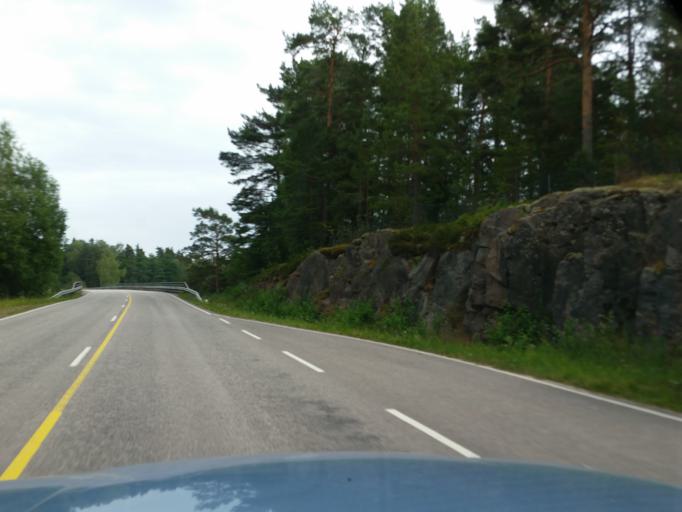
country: FI
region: Varsinais-Suomi
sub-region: Aboland-Turunmaa
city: Nagu
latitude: 60.1750
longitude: 21.9417
